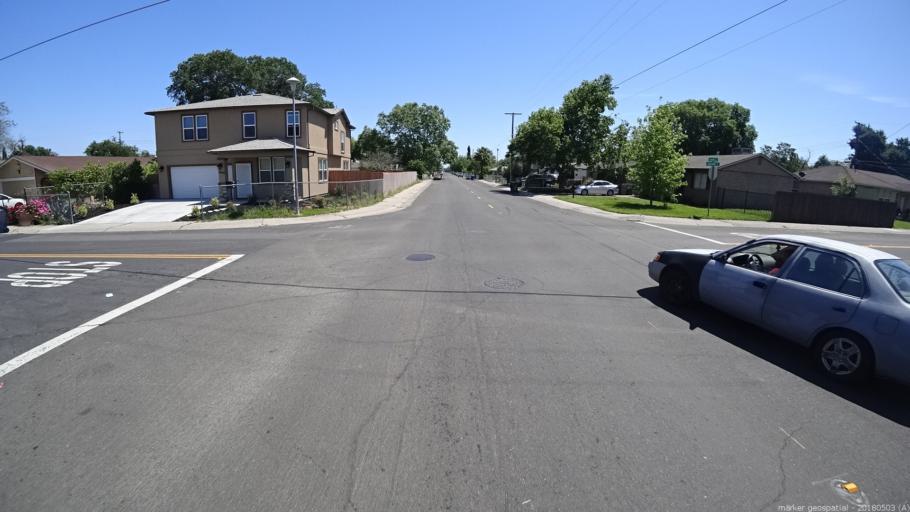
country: US
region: California
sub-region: Sacramento County
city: Arden-Arcade
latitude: 38.6329
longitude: -121.4291
